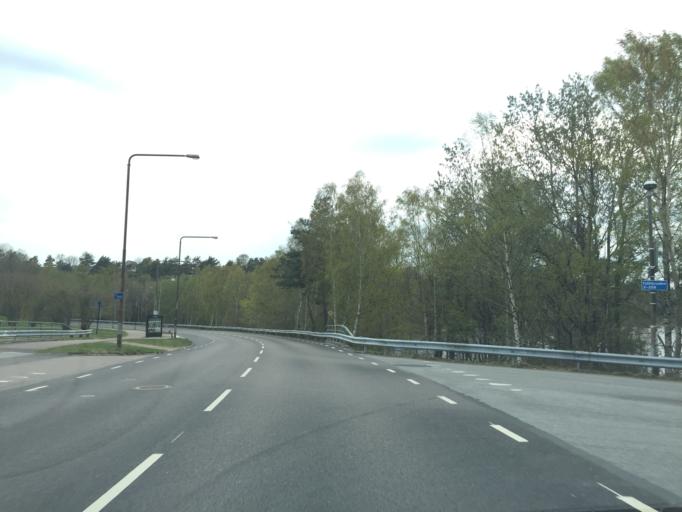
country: SE
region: Vaestra Goetaland
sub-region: Goteborg
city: Rannebergen
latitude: 57.8044
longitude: 12.0747
